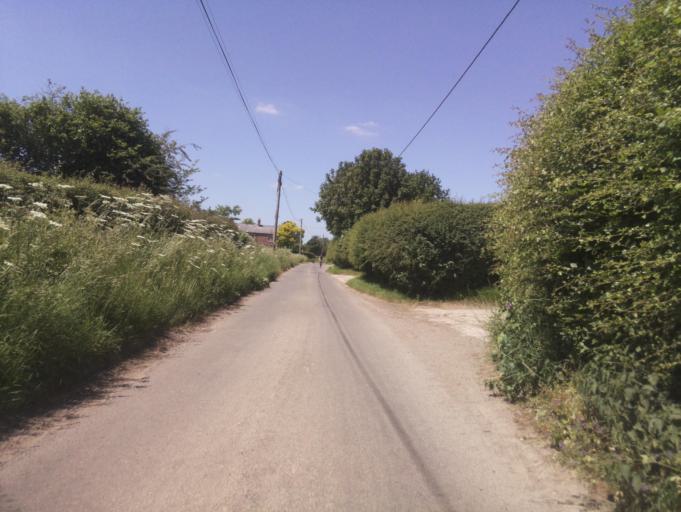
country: GB
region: England
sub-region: Wiltshire
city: Bremhill
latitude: 51.4658
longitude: -2.0743
